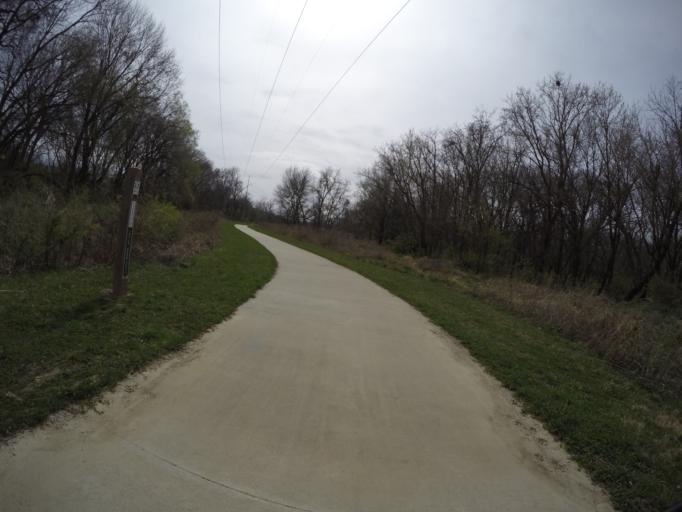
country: US
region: Kansas
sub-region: Johnson County
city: Leawood
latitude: 38.9514
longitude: -94.5774
